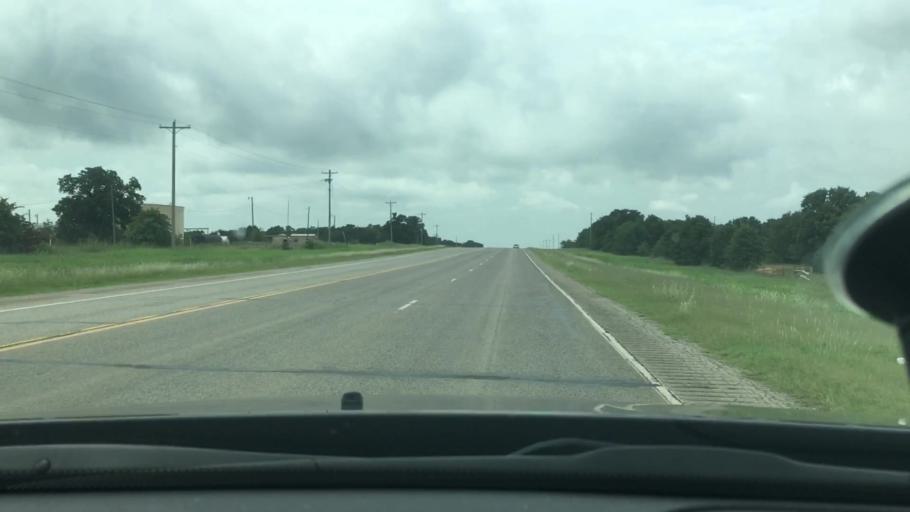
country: US
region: Oklahoma
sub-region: Carter County
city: Healdton
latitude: 34.1987
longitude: -97.4748
